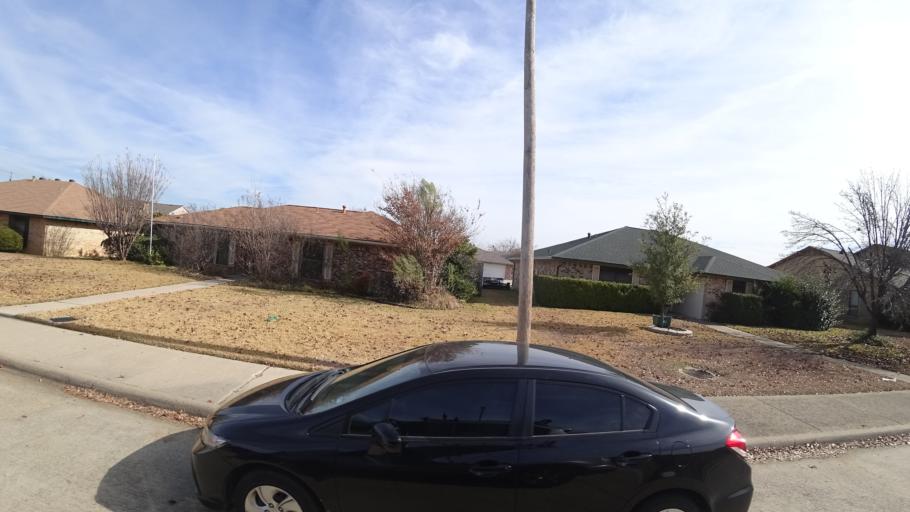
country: US
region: Texas
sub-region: Denton County
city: Highland Village
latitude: 33.0730
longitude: -97.0404
